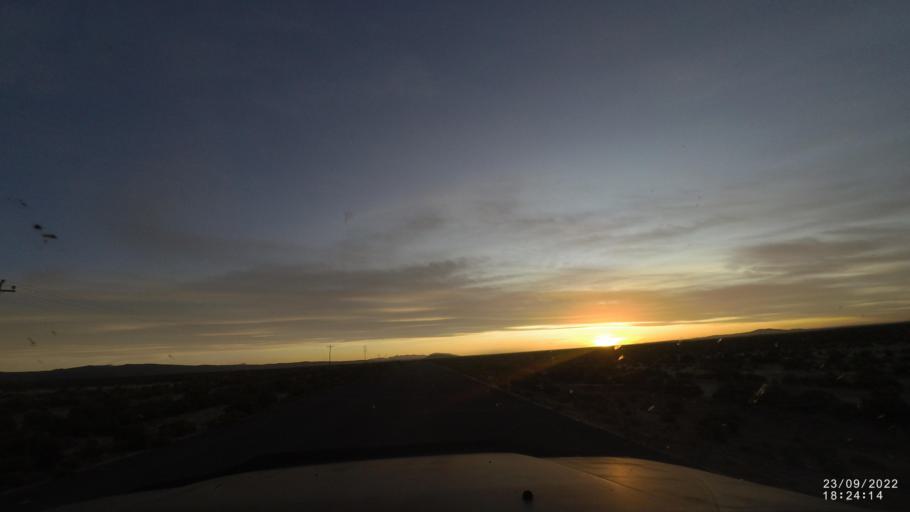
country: BO
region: Oruro
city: Challapata
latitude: -19.3012
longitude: -67.1174
